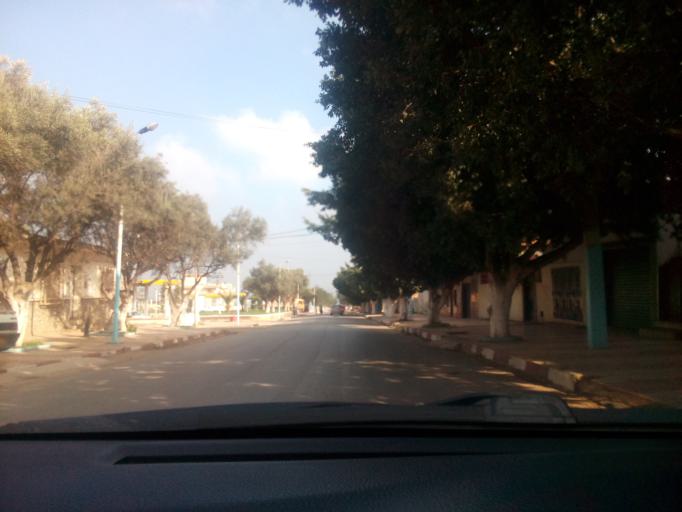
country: DZ
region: Oran
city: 'Ain el Turk
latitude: 35.7031
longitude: -0.8092
